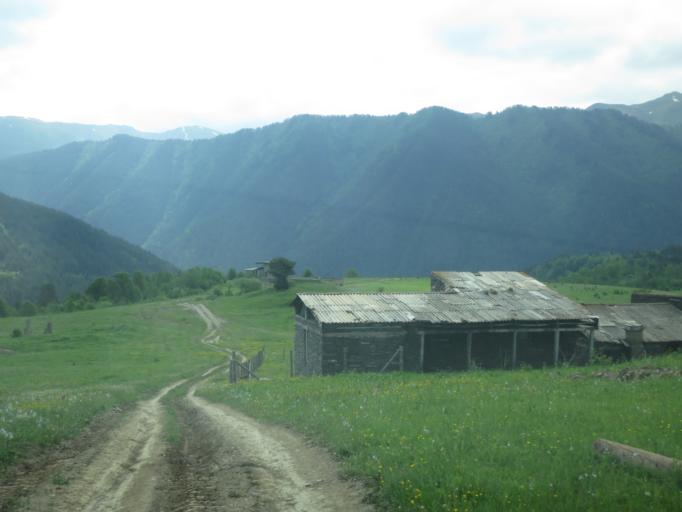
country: RU
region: Chechnya
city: Itum-Kali
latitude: 42.3681
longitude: 45.6378
